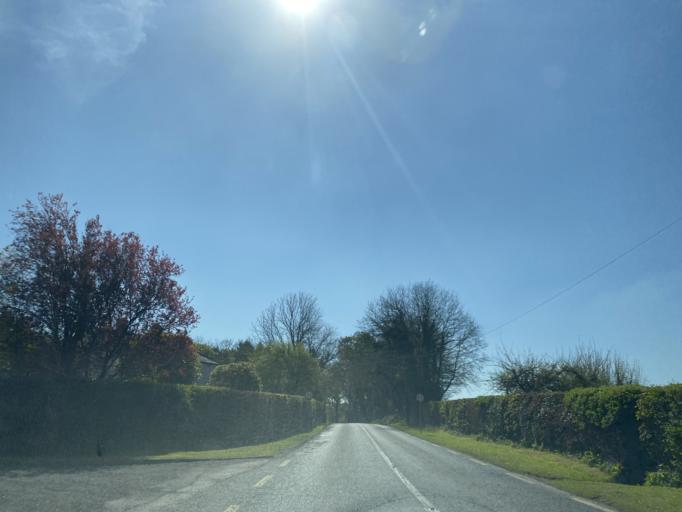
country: IE
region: Leinster
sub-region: Kildare
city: Kill
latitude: 53.3038
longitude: -6.6136
